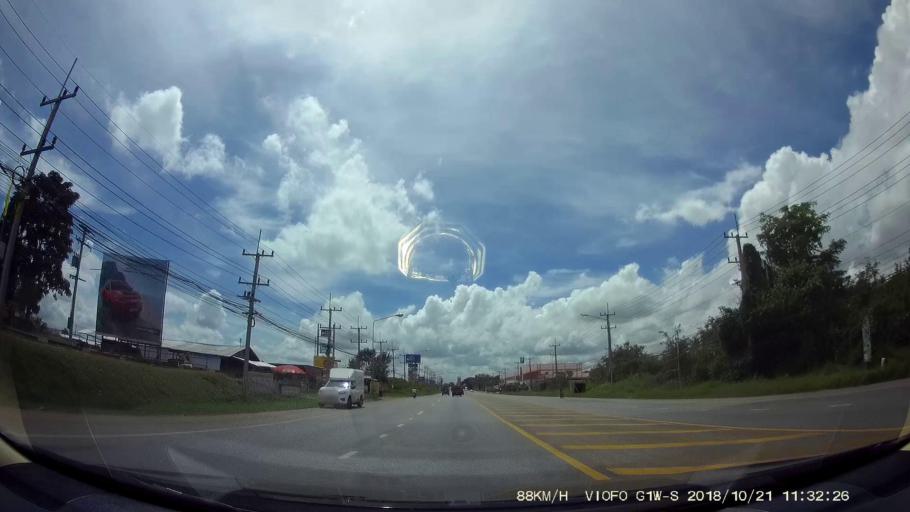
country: TH
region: Chaiyaphum
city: Chaiyaphum
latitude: 15.7587
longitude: 102.0244
